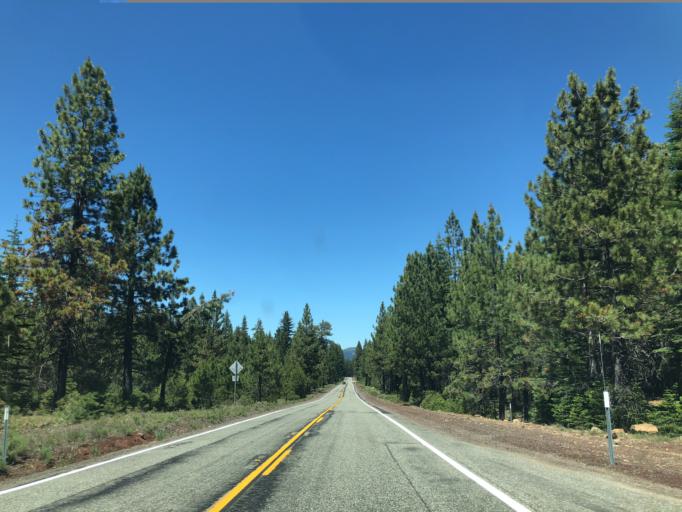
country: US
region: California
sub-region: Shasta County
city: Shingletown
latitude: 40.5626
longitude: -121.5758
